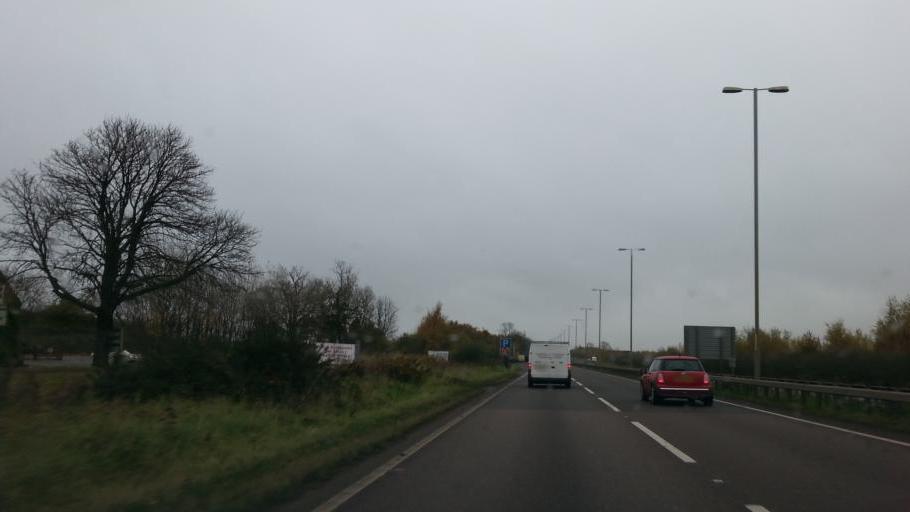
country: GB
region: England
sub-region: Lincolnshire
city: Skellingthorpe
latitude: 53.1567
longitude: -0.6703
